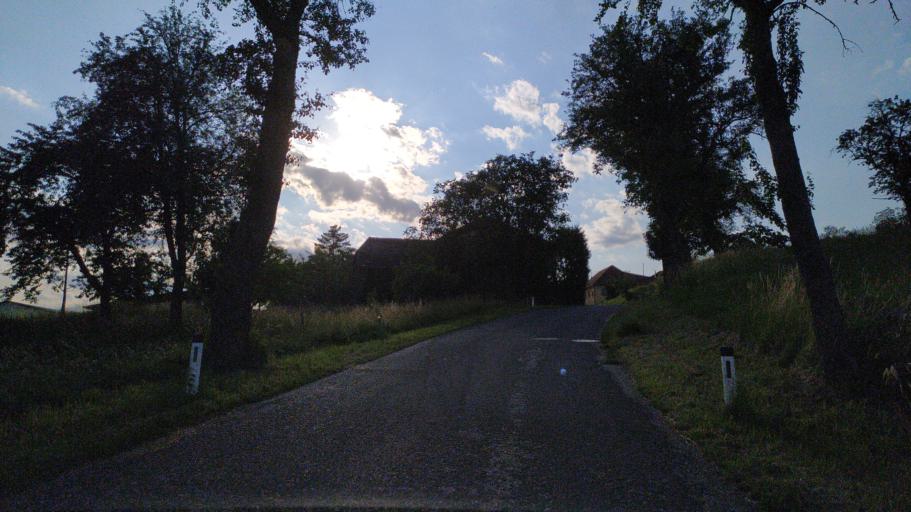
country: AT
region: Lower Austria
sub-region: Politischer Bezirk Amstetten
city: Strengberg
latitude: 48.1497
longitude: 14.6731
